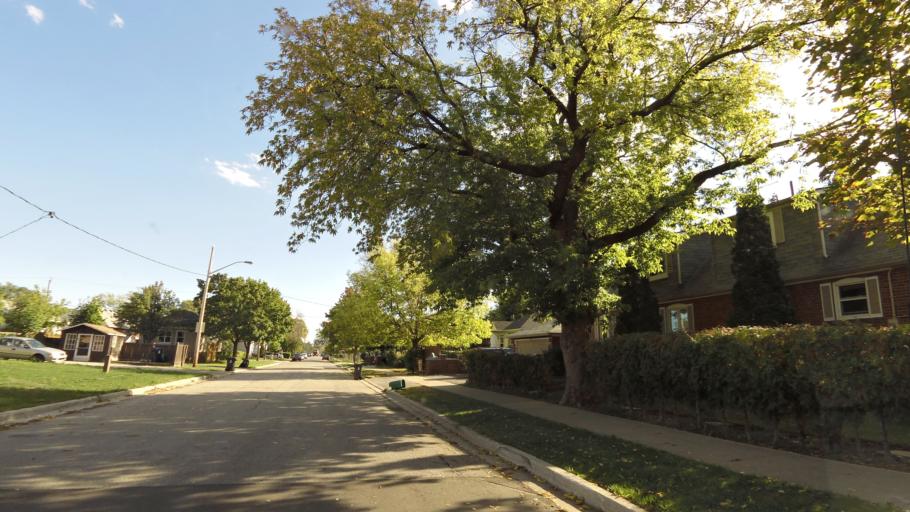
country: CA
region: Ontario
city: Etobicoke
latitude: 43.6222
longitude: -79.4976
